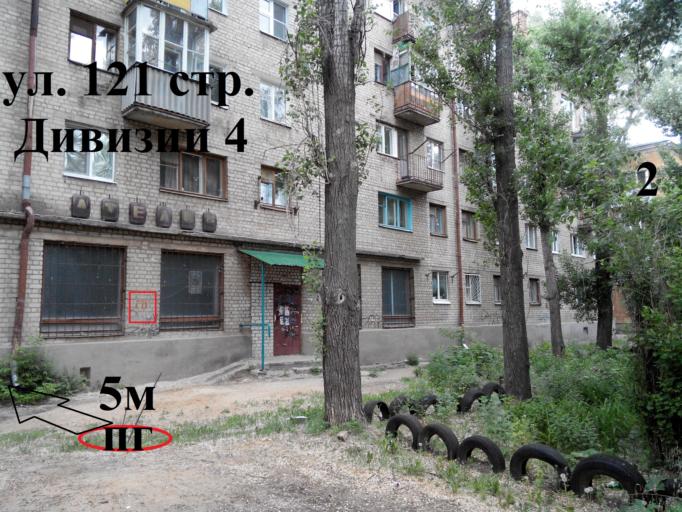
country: RU
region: Voronezj
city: Voronezh
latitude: 51.6464
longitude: 39.1677
